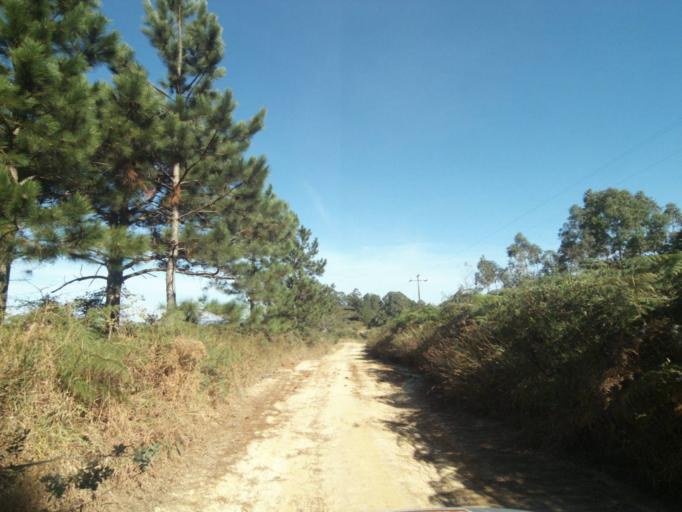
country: BR
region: Parana
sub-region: Tibagi
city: Tibagi
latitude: -24.5670
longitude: -50.4708
